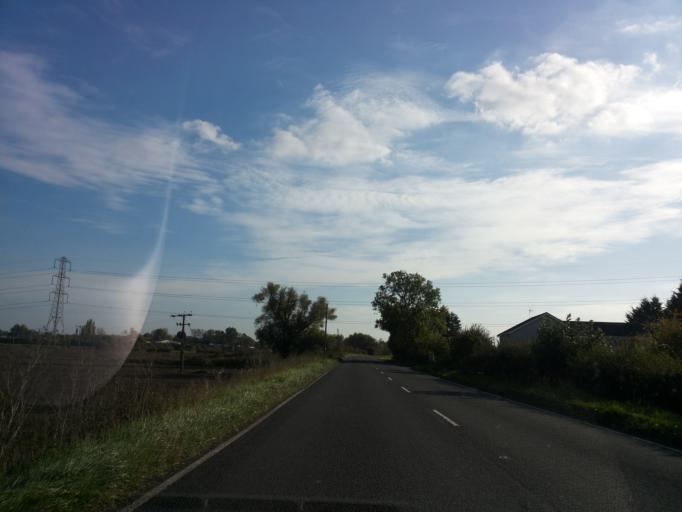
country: GB
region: England
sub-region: Doncaster
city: Hatfield
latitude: 53.6284
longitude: -0.9809
